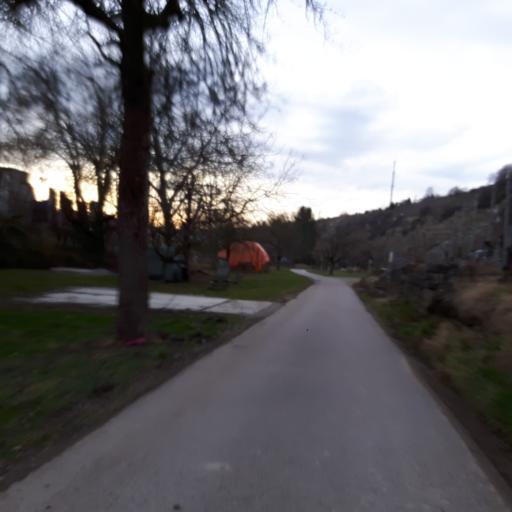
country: DE
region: Baden-Wuerttemberg
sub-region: Regierungsbezirk Stuttgart
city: Benningen am Neckar
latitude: 48.9513
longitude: 9.2402
